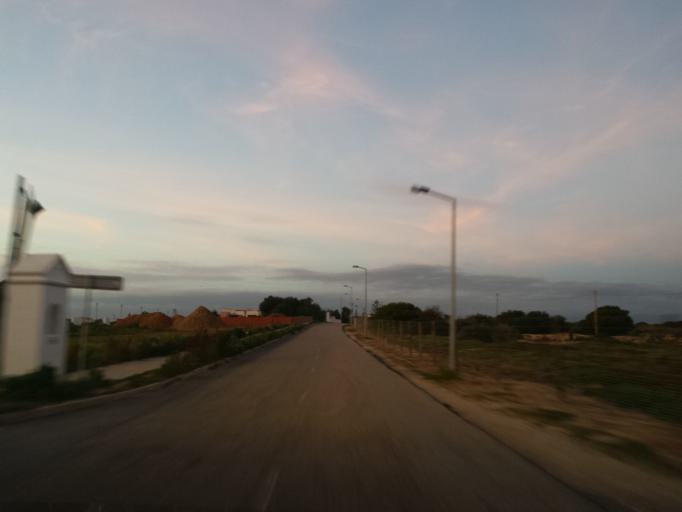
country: PT
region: Faro
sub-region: Lagos
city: Lagos
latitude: 37.0866
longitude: -8.6711
